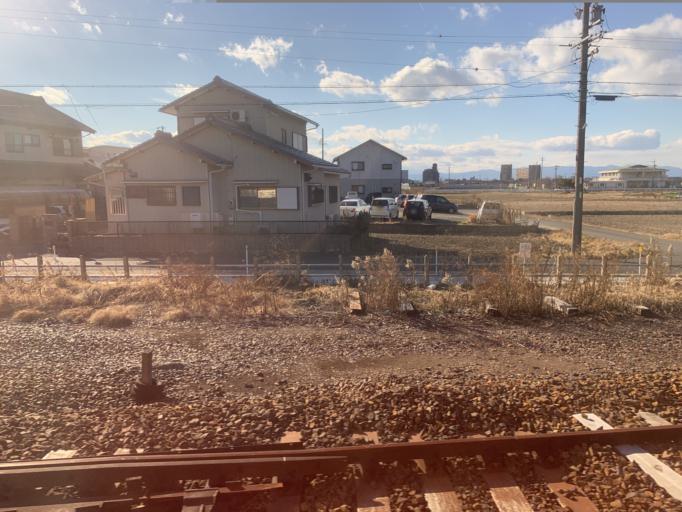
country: JP
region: Aichi
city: Inazawa
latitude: 35.2618
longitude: 136.8167
